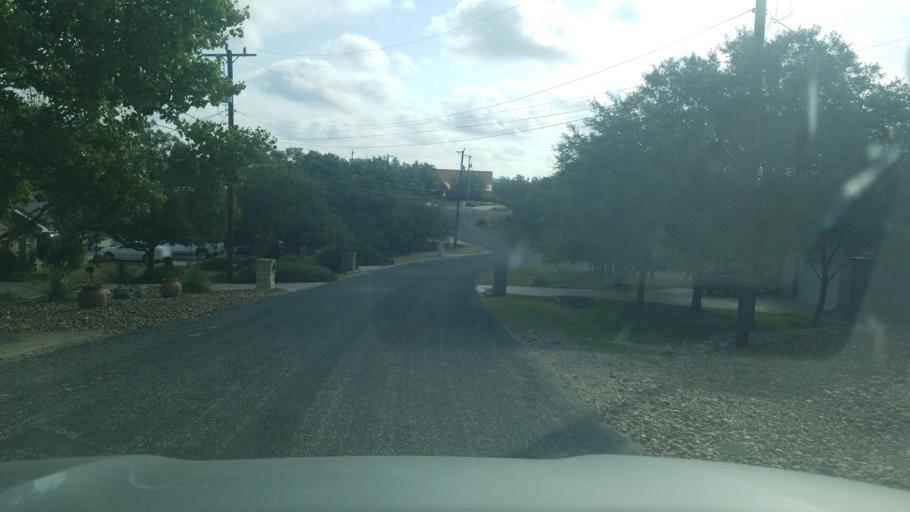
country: US
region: Texas
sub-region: Bexar County
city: Timberwood Park
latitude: 29.6856
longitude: -98.5058
